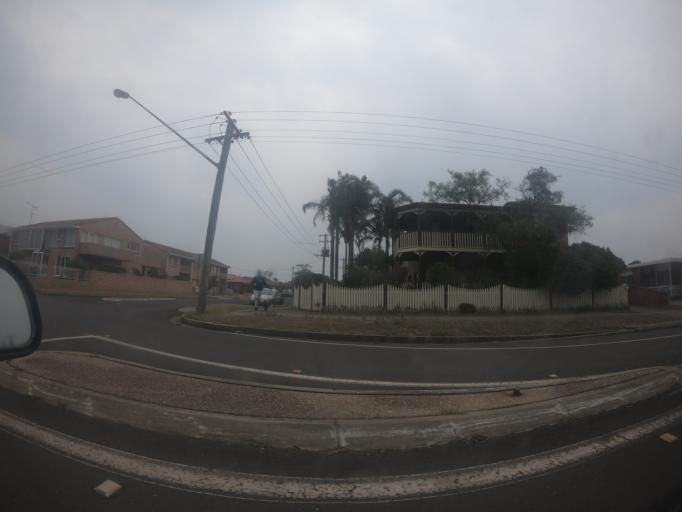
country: AU
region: New South Wales
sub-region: Shellharbour
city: Lake Illawarra
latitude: -34.5429
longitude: 150.8678
